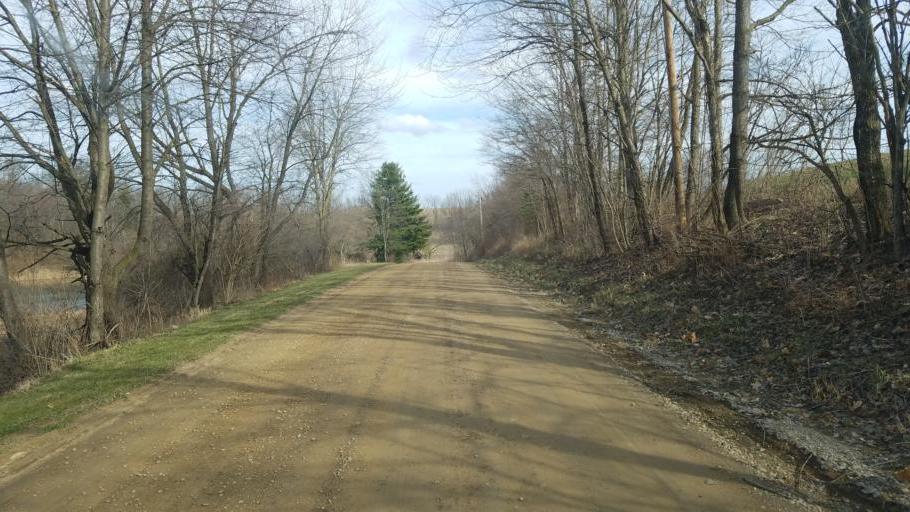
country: US
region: Ohio
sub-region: Knox County
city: Danville
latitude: 40.5442
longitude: -82.3567
